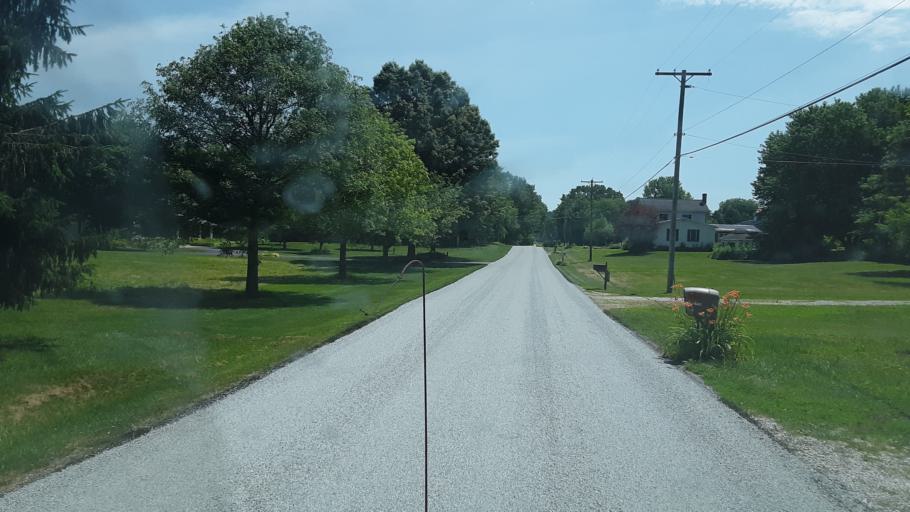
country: US
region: Ohio
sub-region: Wayne County
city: Shreve
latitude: 40.7190
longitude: -81.9546
